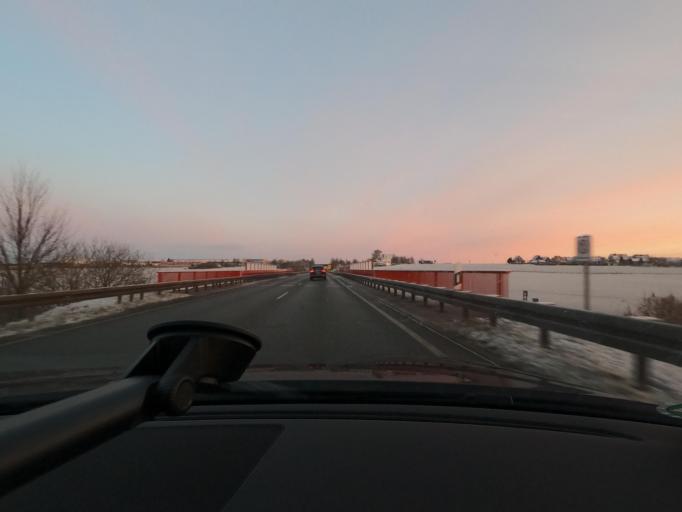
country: DE
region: Thuringia
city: Hausen
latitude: 51.3838
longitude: 10.3467
